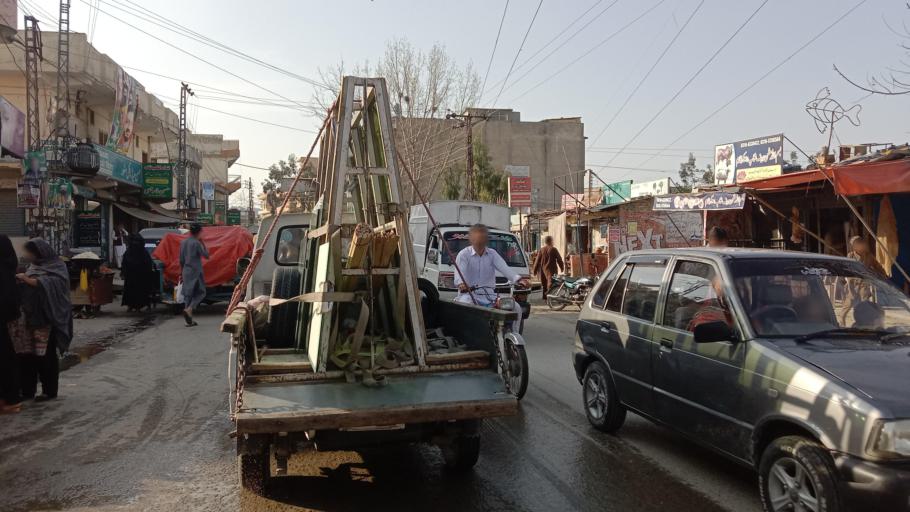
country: PK
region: Khyber Pakhtunkhwa
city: Abbottabad
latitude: 34.1966
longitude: 73.2338
